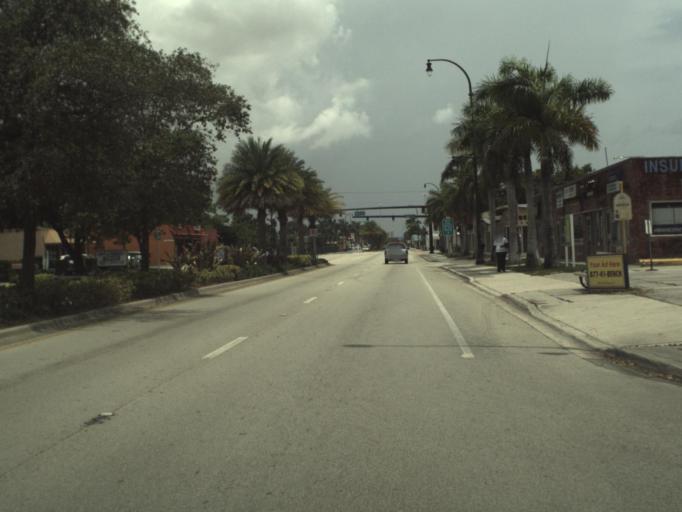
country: US
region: Florida
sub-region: Broward County
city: Hallandale Beach
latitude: 25.9879
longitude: -80.1424
